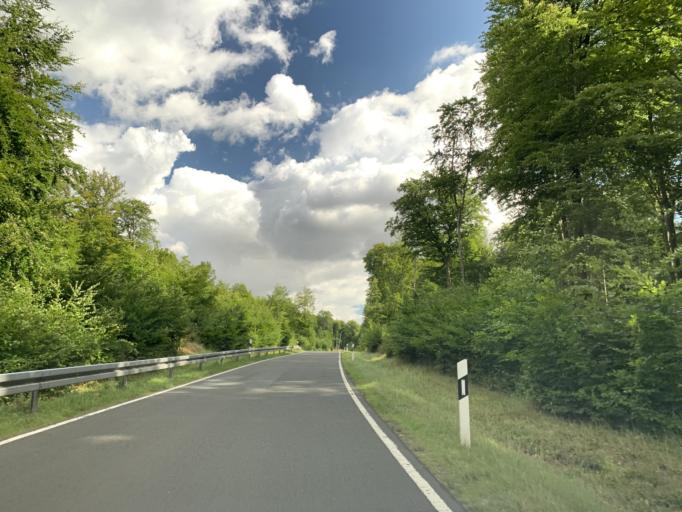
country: DE
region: Mecklenburg-Vorpommern
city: Wustrow
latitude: 53.4053
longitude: 13.1640
